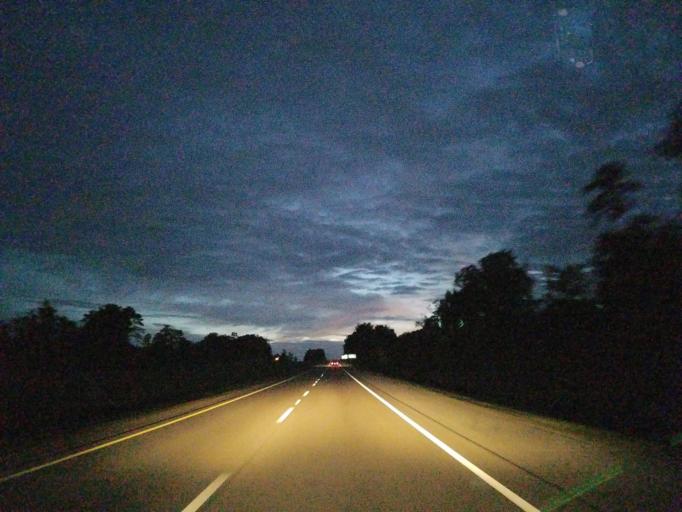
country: US
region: Mississippi
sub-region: Jones County
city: Sharon
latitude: 31.7394
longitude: -89.0882
